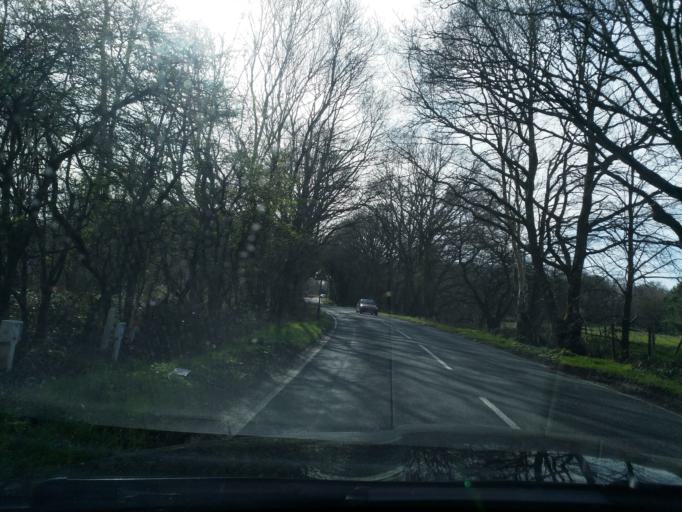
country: GB
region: England
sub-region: Hampshire
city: Farnborough
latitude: 51.2830
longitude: -0.7877
